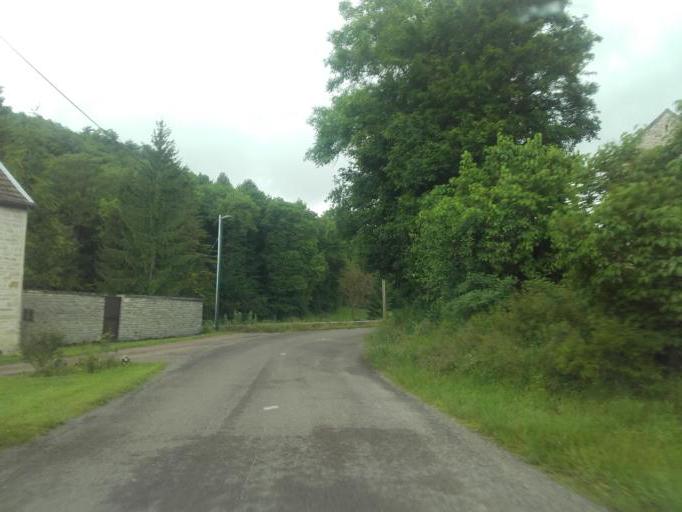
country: FR
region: Bourgogne
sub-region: Departement de la Cote-d'Or
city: Meursault
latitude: 47.0222
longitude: 4.7362
